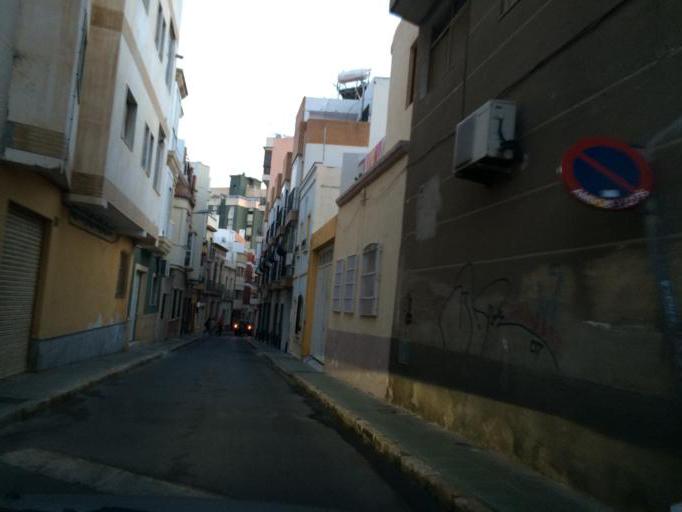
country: ES
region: Andalusia
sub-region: Provincia de Almeria
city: Almeria
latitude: 36.8442
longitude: -2.4655
